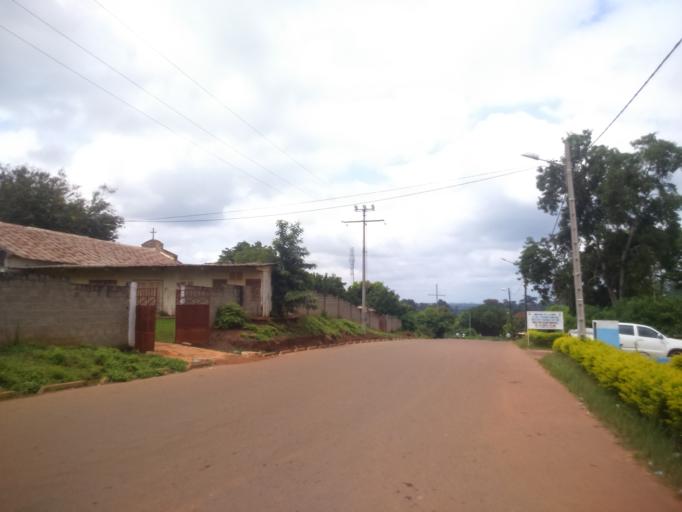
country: CI
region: Fromager
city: Oume
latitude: 6.3779
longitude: -5.4193
